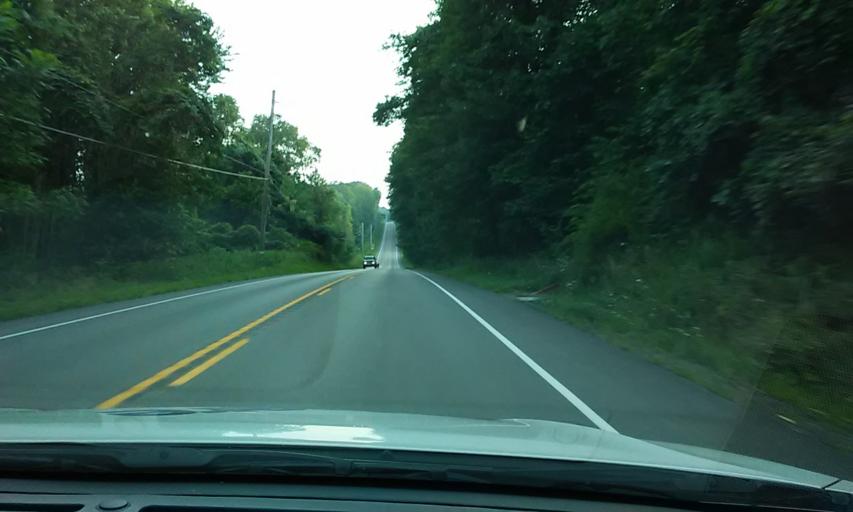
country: US
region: Pennsylvania
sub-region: Forest County
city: Marienville
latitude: 41.5012
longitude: -79.0810
